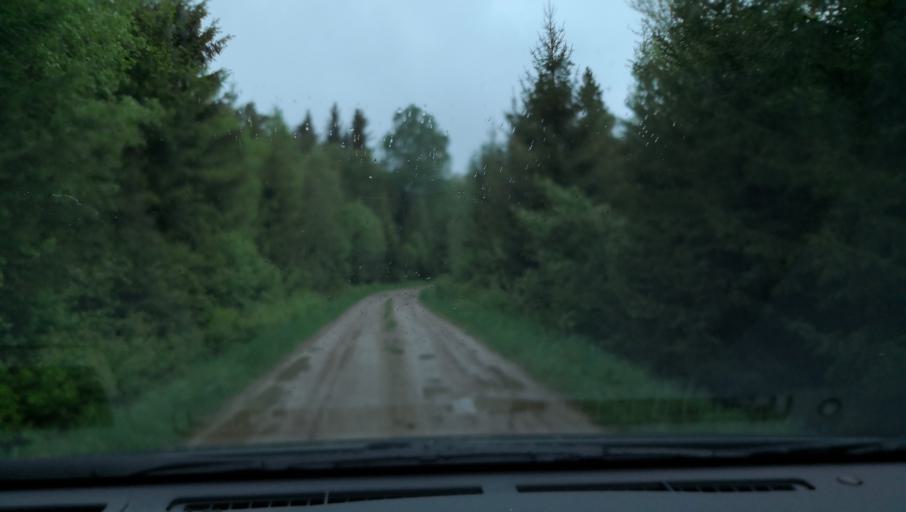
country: SE
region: Uppsala
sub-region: Enkopings Kommun
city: Orsundsbro
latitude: 59.9200
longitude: 17.3446
